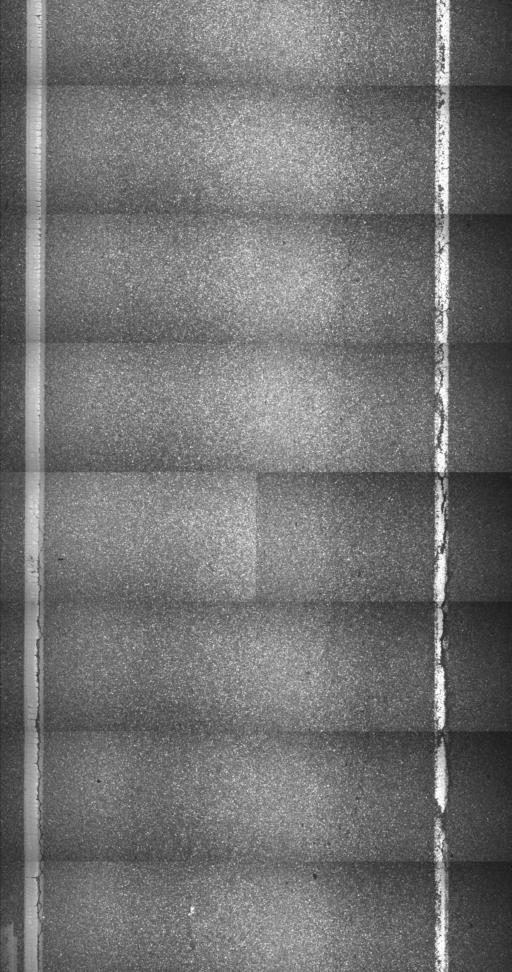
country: US
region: Vermont
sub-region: Franklin County
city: Saint Albans
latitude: 44.7631
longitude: -73.0811
